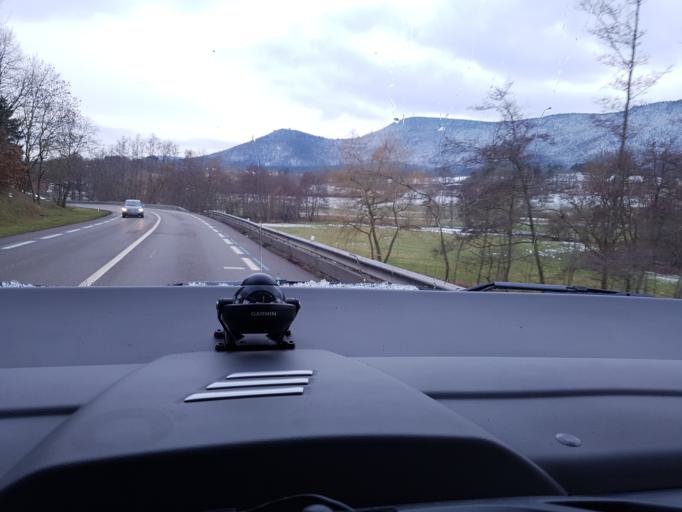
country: FR
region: Alsace
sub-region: Departement du Bas-Rhin
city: Ville
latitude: 48.3297
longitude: 7.3311
